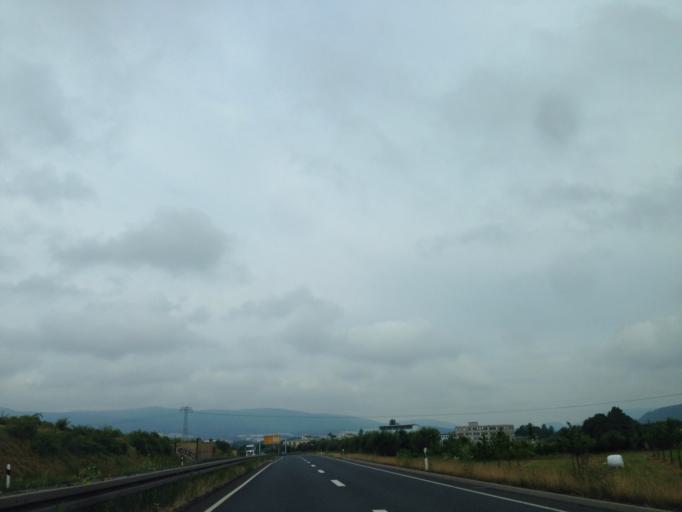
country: DE
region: Thuringia
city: Saalfeld
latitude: 50.6590
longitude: 11.3883
